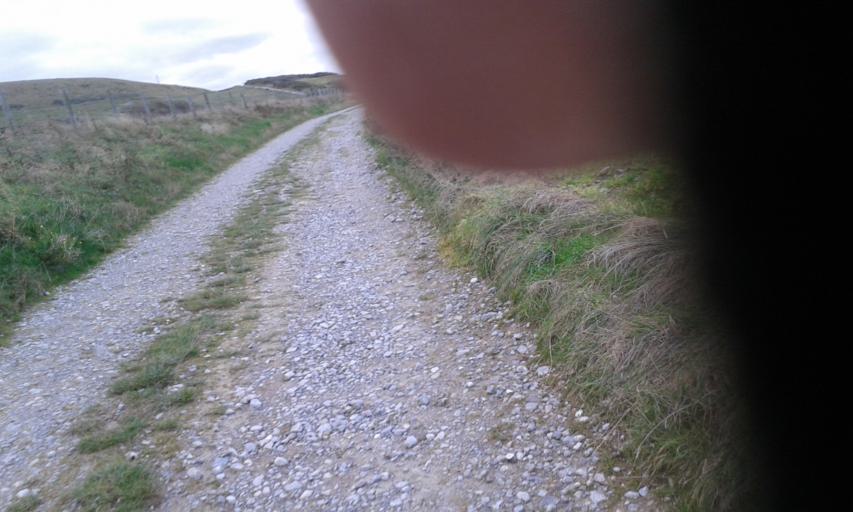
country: FR
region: Nord-Pas-de-Calais
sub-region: Departement du Pas-de-Calais
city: Sangatte
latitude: 50.9391
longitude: 1.7372
